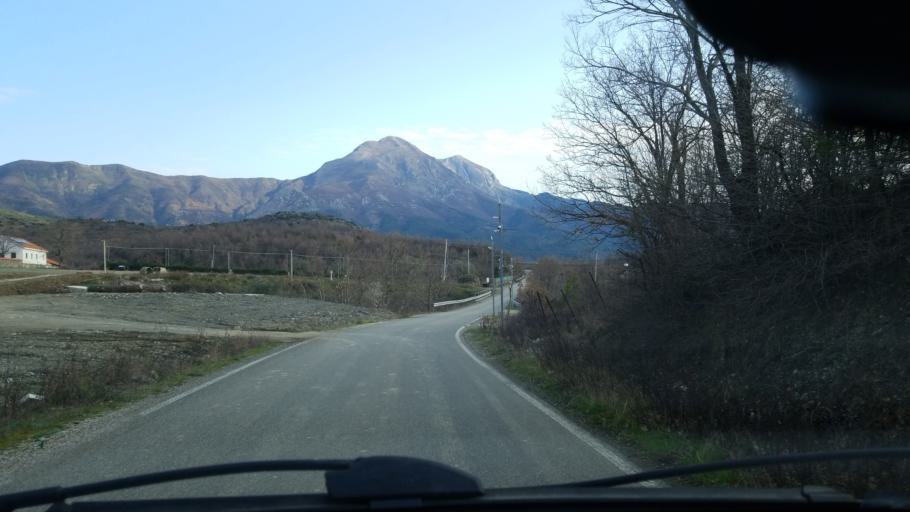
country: AL
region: Lezhe
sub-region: Rrethi i Lezhes
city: Kallmeti i Madh
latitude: 41.8817
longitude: 19.6918
